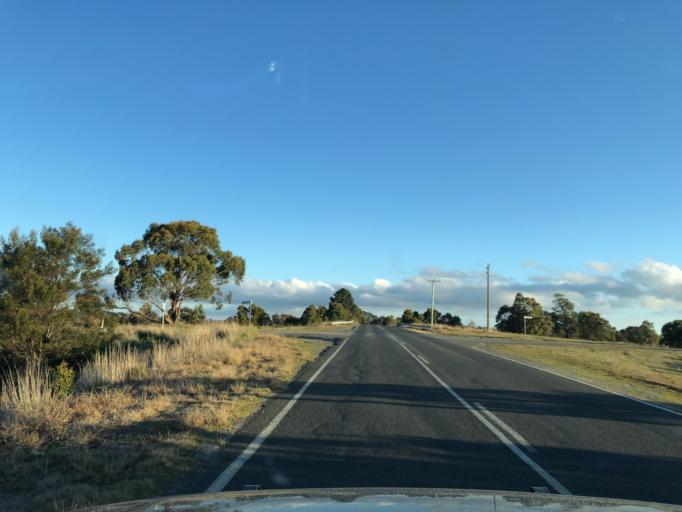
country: AU
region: Victoria
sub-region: Moorabool
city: Bacchus Marsh
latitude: -37.5886
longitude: 144.2361
